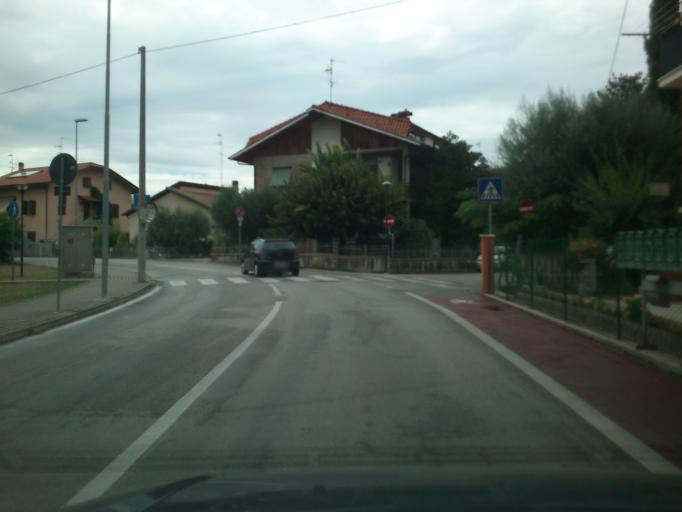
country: IT
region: The Marches
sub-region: Provincia di Pesaro e Urbino
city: Lucrezia
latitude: 43.7730
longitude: 12.9389
